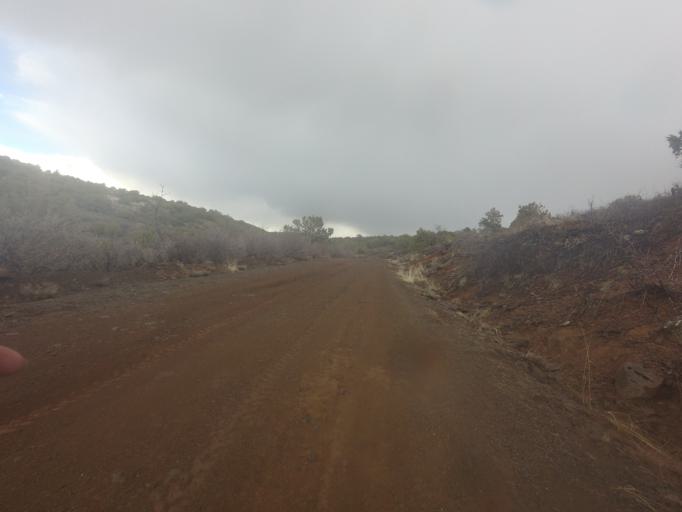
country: US
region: Arizona
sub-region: Gila County
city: Pine
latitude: 34.4031
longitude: -111.5718
